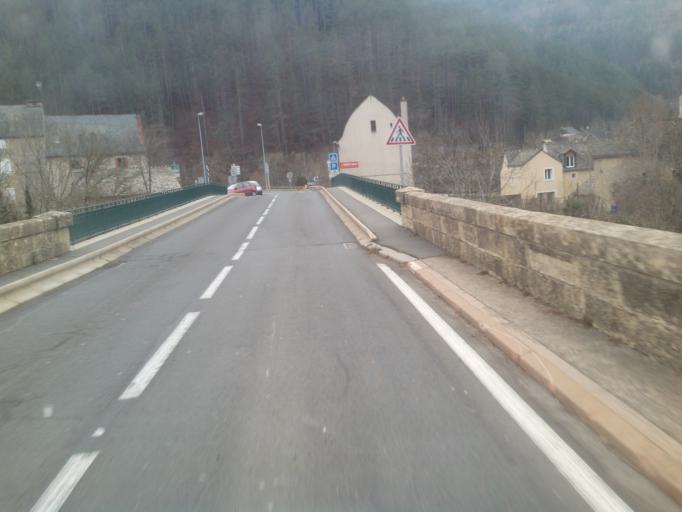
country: FR
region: Languedoc-Roussillon
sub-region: Departement de la Lozere
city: Mende
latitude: 44.4813
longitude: 3.4566
